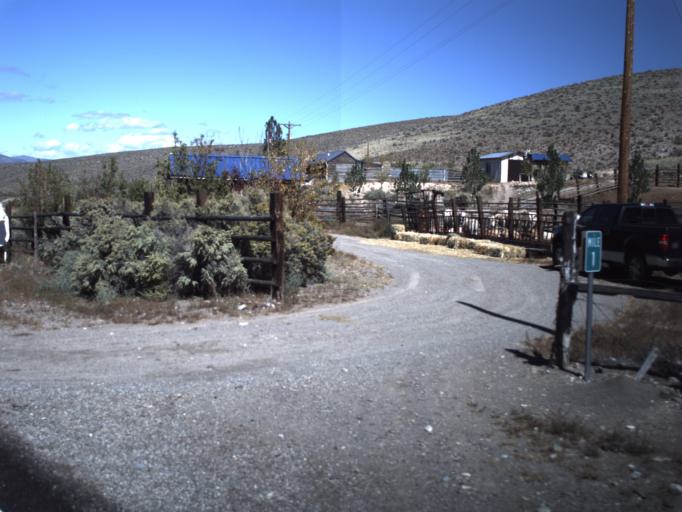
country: US
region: Utah
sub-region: Piute County
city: Junction
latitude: 38.1024
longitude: -111.9846
